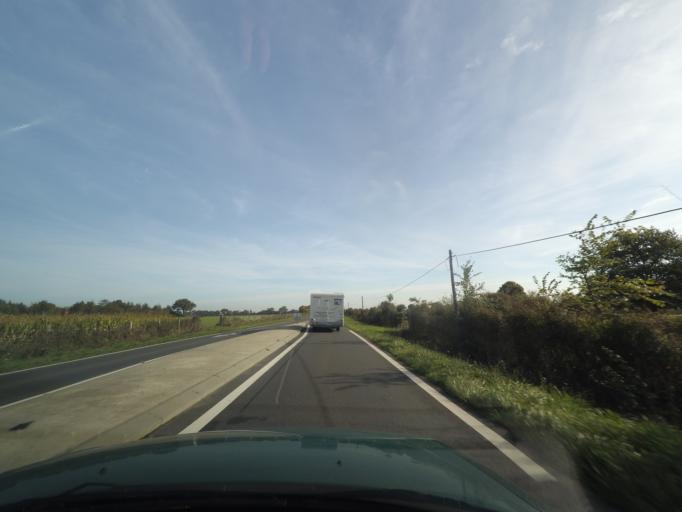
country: FR
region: Pays de la Loire
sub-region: Departement de Maine-et-Loire
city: Torfou
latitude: 47.0361
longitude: -1.0853
